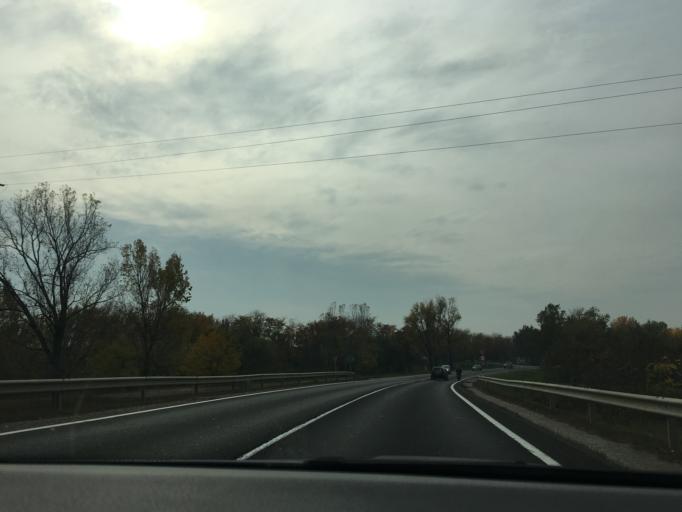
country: HU
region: Hajdu-Bihar
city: Debrecen
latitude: 47.5064
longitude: 21.5933
